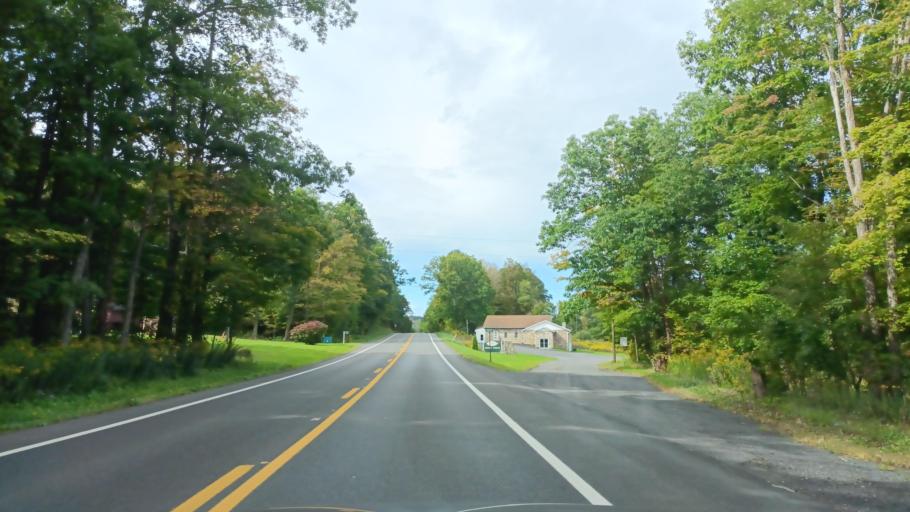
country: US
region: Maryland
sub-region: Garrett County
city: Mountain Lake Park
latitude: 39.2731
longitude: -79.2516
